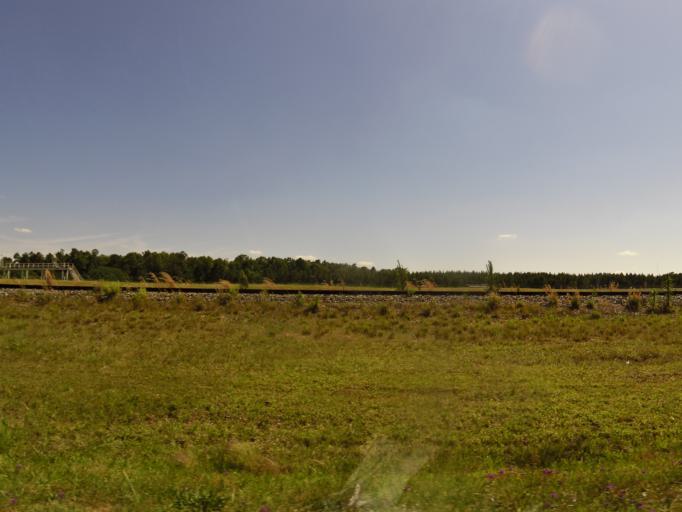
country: US
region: South Carolina
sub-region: Aiken County
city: Aiken
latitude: 33.5210
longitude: -81.6064
